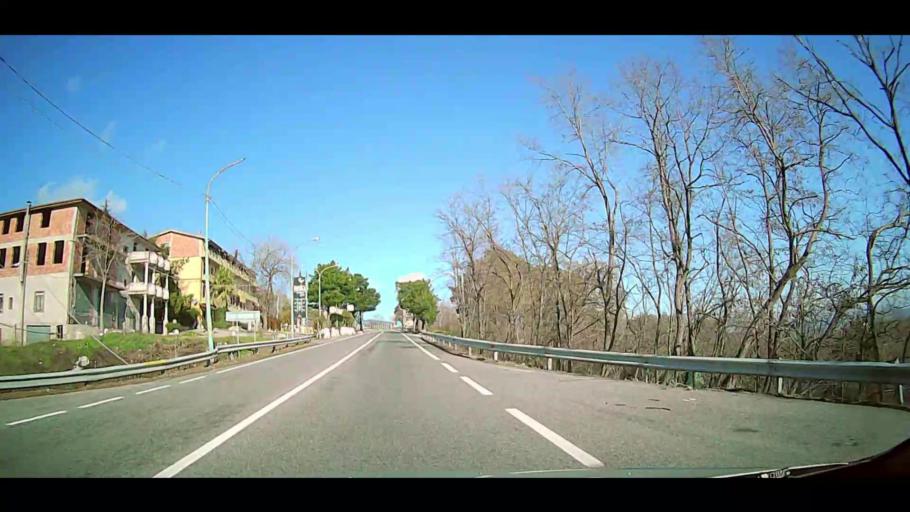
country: IT
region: Calabria
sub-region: Provincia di Crotone
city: Cerenzia
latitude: 39.2455
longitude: 16.7904
